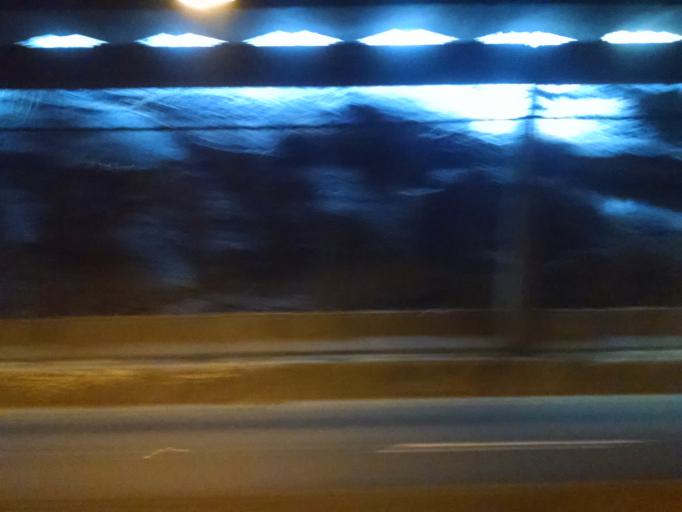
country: BR
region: Rio de Janeiro
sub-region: Rio De Janeiro
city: Rio de Janeiro
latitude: -22.9805
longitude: -43.2318
